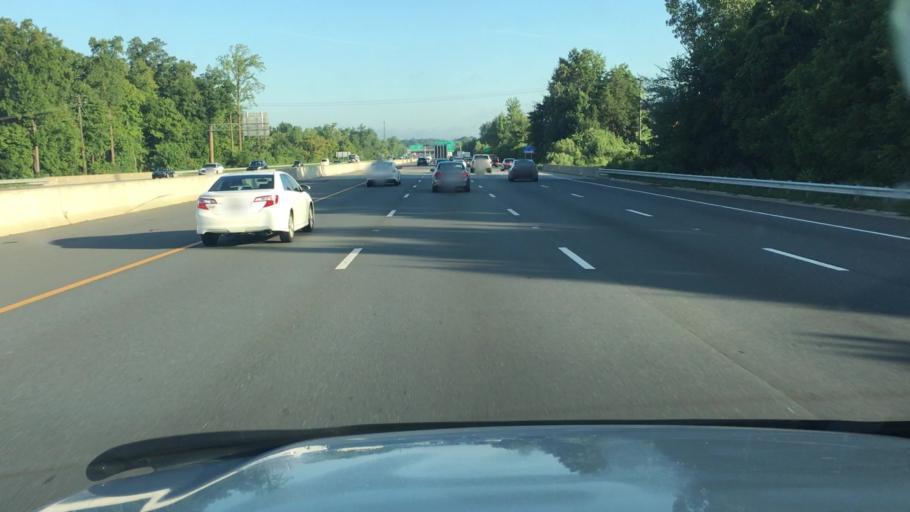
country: US
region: North Carolina
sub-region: Mecklenburg County
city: Pineville
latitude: 35.1109
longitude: -80.8970
